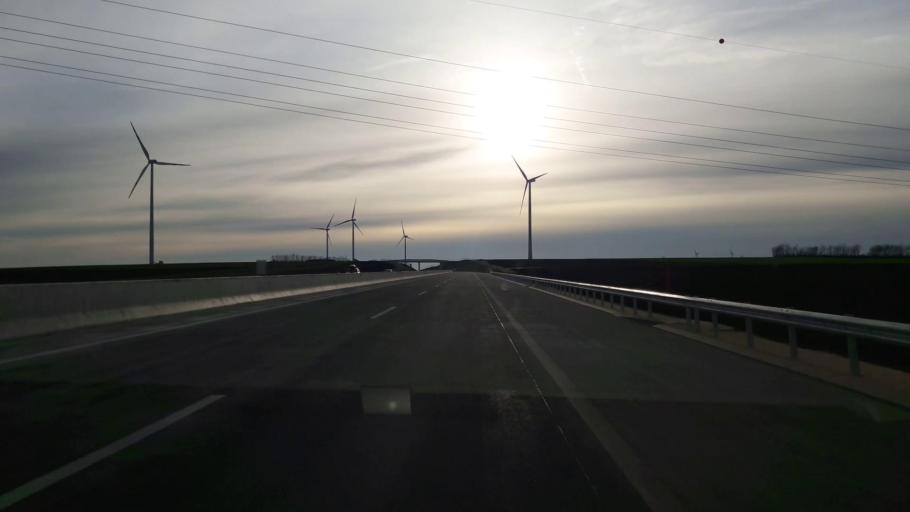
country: AT
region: Lower Austria
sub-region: Politischer Bezirk Mistelbach
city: Grosskrut
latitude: 48.6351
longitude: 16.6811
